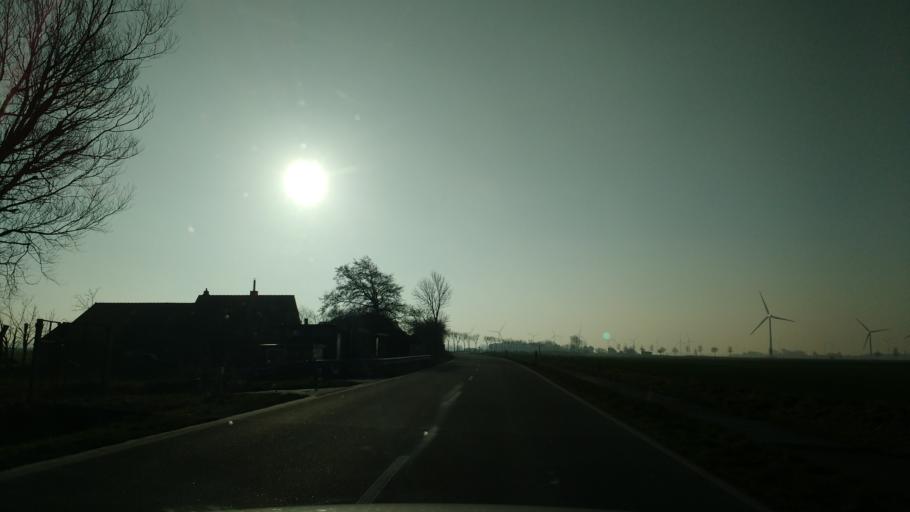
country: DE
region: Schleswig-Holstein
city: Helse
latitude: 53.9900
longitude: 8.9948
